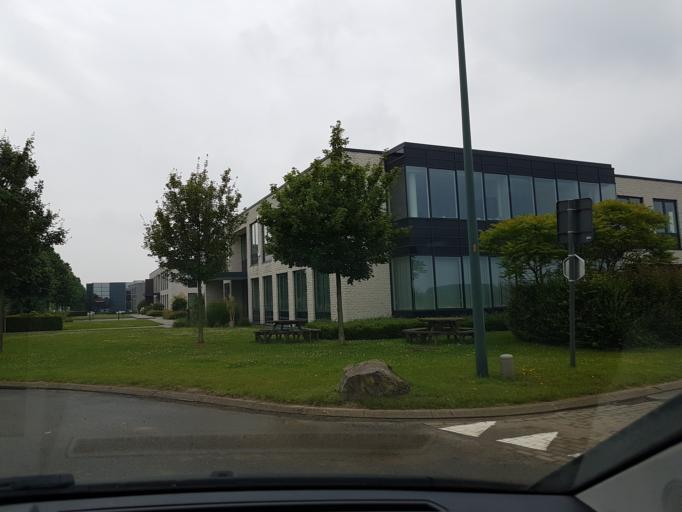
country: BE
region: Flanders
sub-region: Provincie Vlaams-Brabant
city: Zaventem
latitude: 50.8776
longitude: 4.4935
